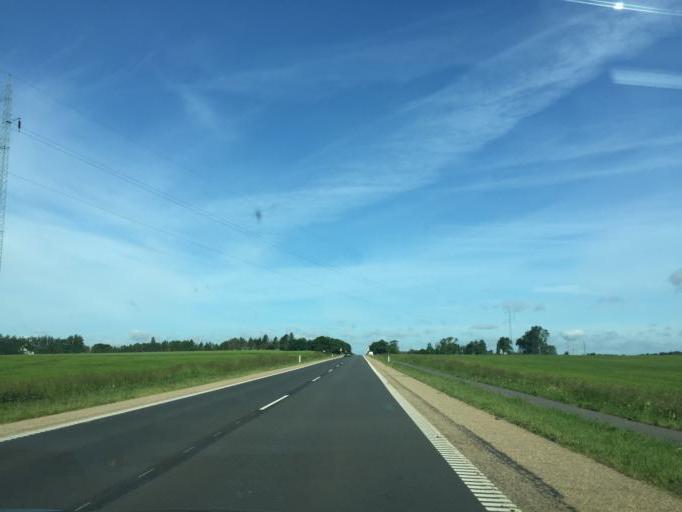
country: DK
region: South Denmark
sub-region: Middelfart Kommune
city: Norre Aby
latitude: 55.4857
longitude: 9.8203
